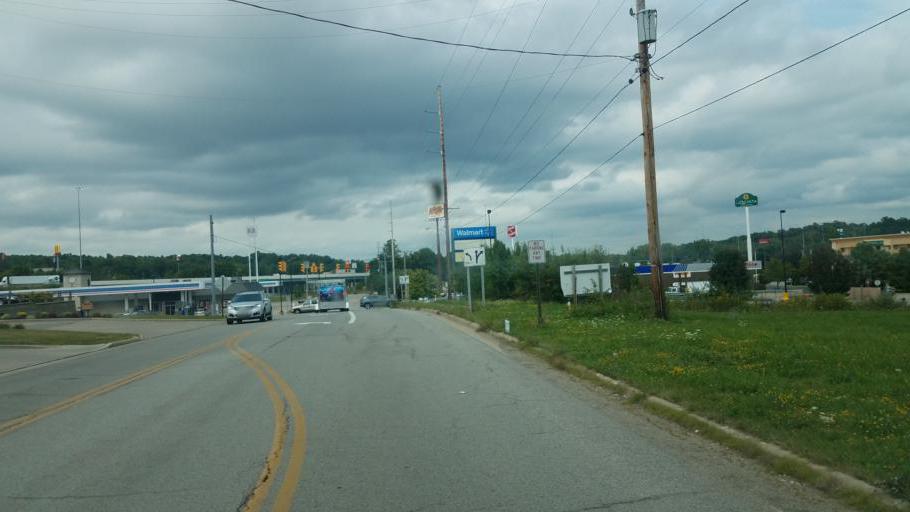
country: US
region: Ohio
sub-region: Richland County
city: Mansfield
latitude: 40.6915
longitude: -82.5113
